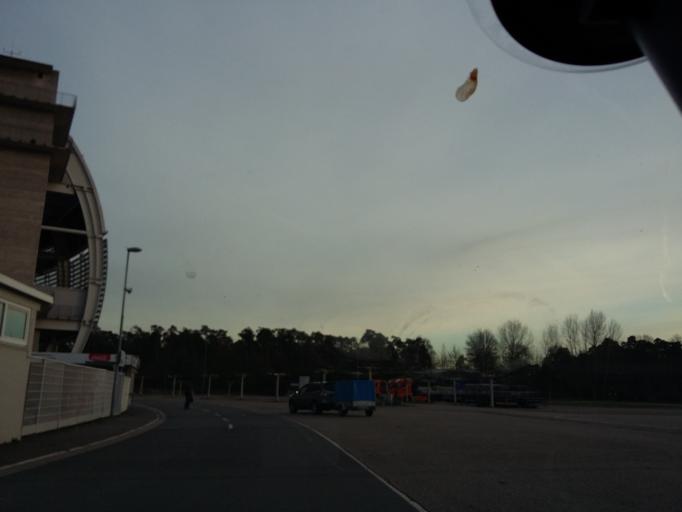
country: DE
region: Baden-Wuerttemberg
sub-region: Karlsruhe Region
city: Hockenheim
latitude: 49.3255
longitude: 8.5664
